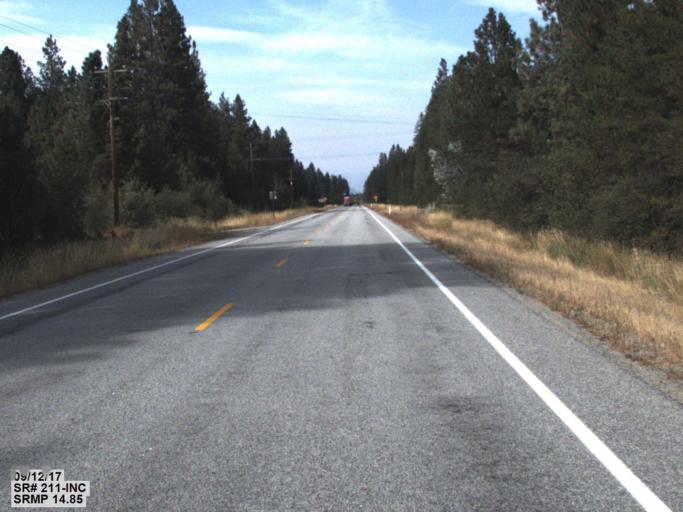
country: US
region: Washington
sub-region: Pend Oreille County
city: Newport
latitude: 48.3004
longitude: -117.2845
